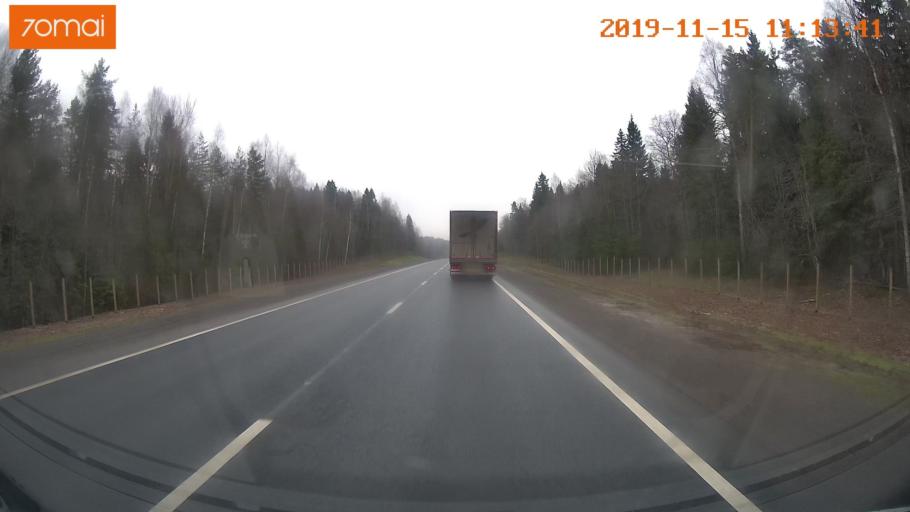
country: RU
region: Vologda
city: Chebsara
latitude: 59.1228
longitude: 39.1727
